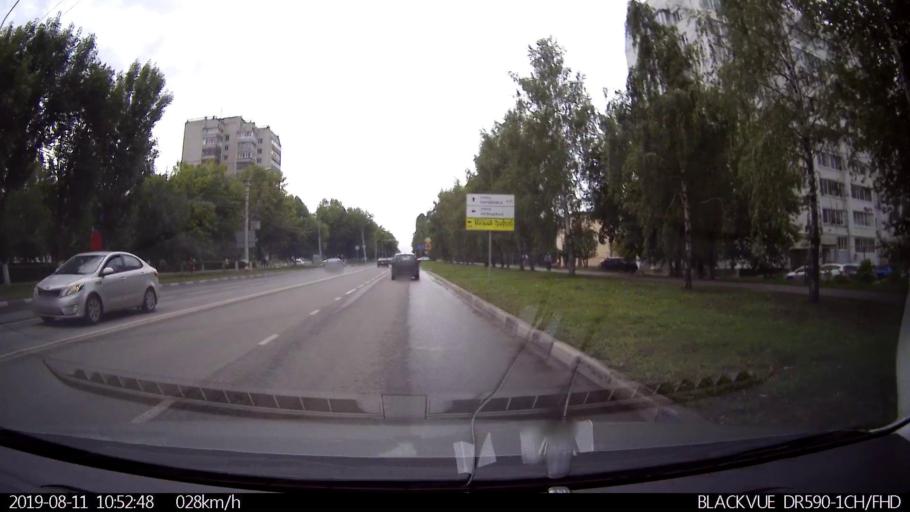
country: RU
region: Ulyanovsk
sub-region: Ulyanovskiy Rayon
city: Ulyanovsk
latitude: 54.2631
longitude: 48.3344
